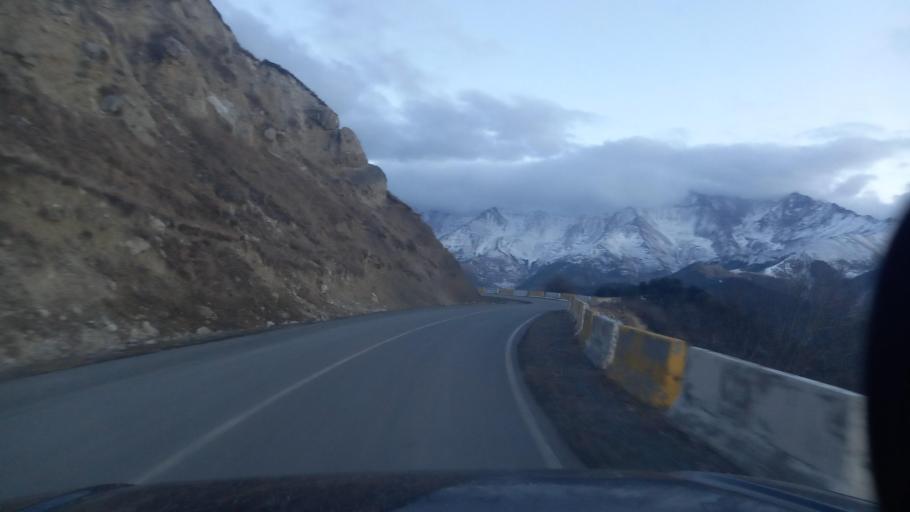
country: RU
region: Ingushetiya
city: Dzhayrakh
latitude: 42.8201
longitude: 44.8349
